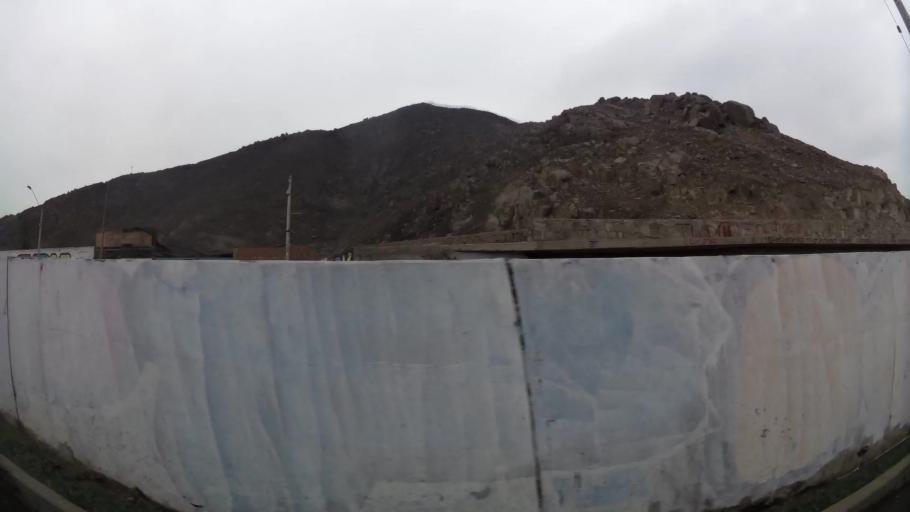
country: PE
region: Lima
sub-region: Lima
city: Vitarte
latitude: -12.0514
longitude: -76.9378
